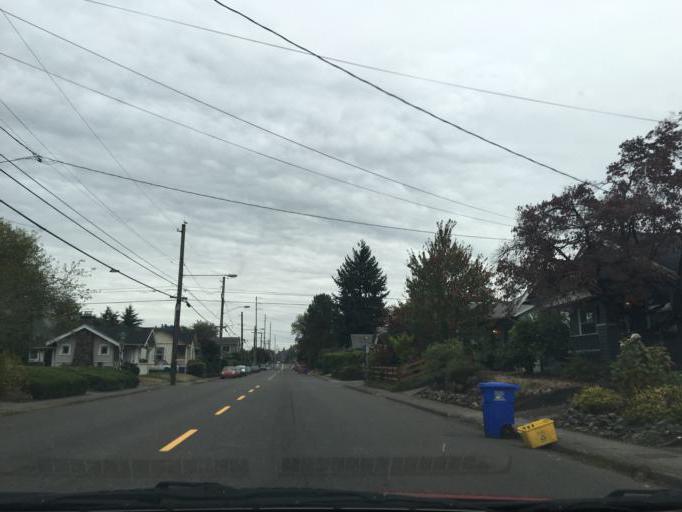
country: US
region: Oregon
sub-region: Multnomah County
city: Lents
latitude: 45.5327
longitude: -122.6022
